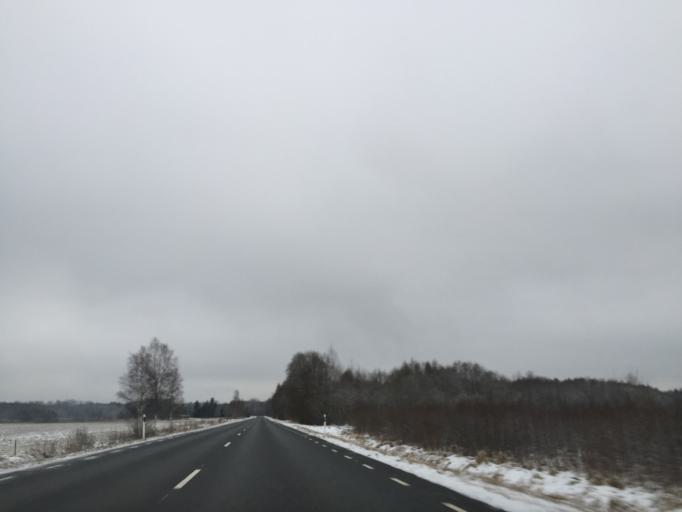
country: EE
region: Laeaene
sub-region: Lihula vald
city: Lihula
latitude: 58.6595
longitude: 23.8363
